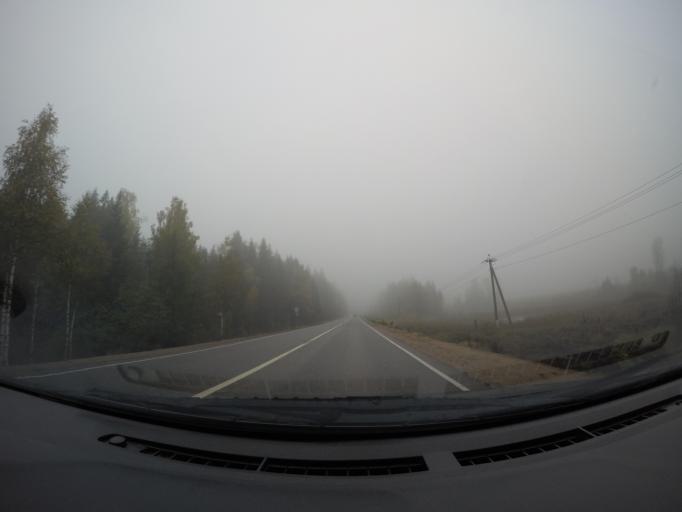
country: RU
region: Moskovskaya
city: Ruza
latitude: 55.7227
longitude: 36.2793
